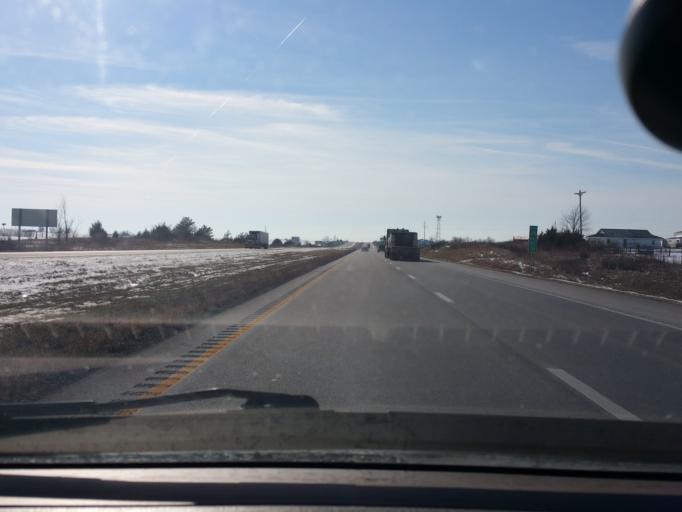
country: US
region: Missouri
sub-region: Clinton County
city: Cameron
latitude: 39.8472
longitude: -94.1798
